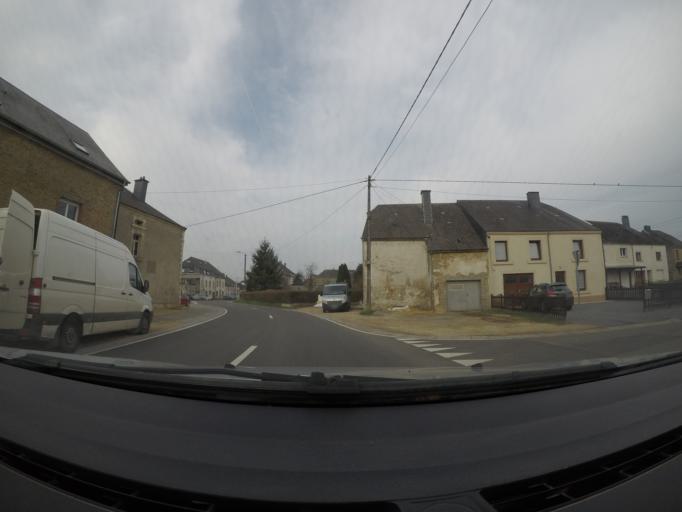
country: BE
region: Wallonia
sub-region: Province du Luxembourg
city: Tintigny
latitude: 49.7045
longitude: 5.4260
